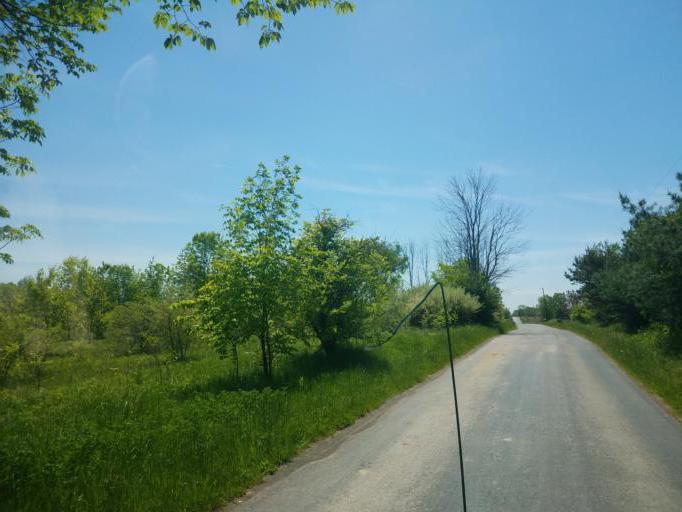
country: US
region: Ohio
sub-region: Wayne County
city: West Salem
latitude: 40.9817
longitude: -82.1772
